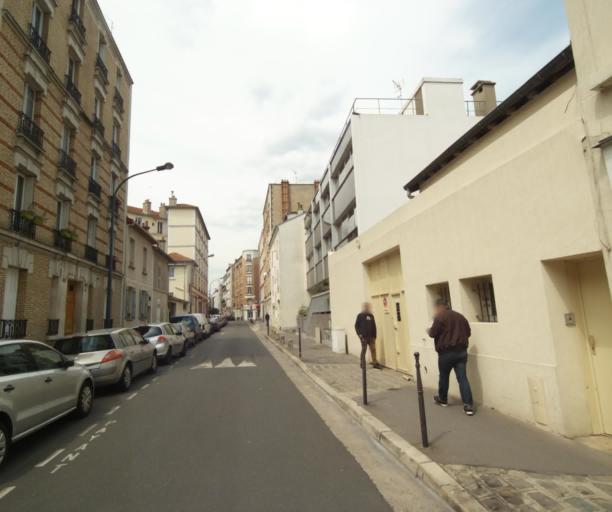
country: FR
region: Ile-de-France
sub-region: Departement des Hauts-de-Seine
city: Asnieres-sur-Seine
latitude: 48.9134
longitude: 2.2944
